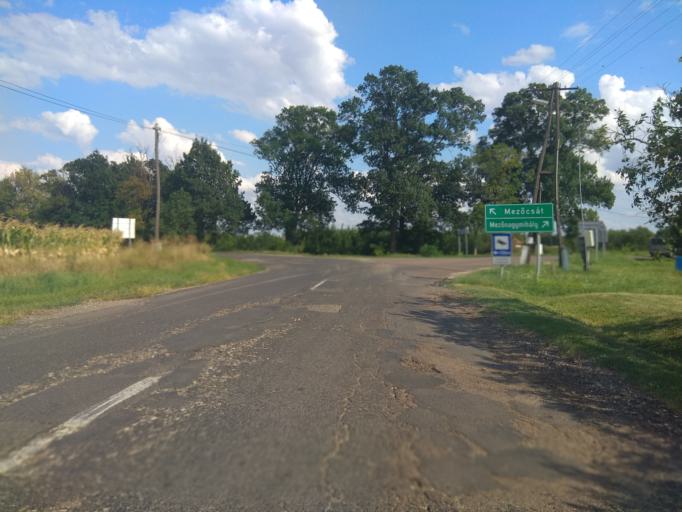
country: HU
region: Borsod-Abauj-Zemplen
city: Mezokeresztes
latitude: 47.8112
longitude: 20.7196
